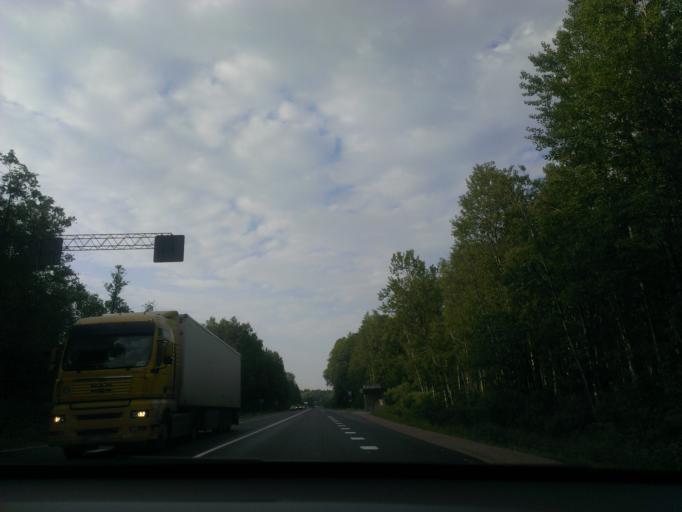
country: LV
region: Kekava
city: Kekava
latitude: 56.7100
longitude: 24.2469
